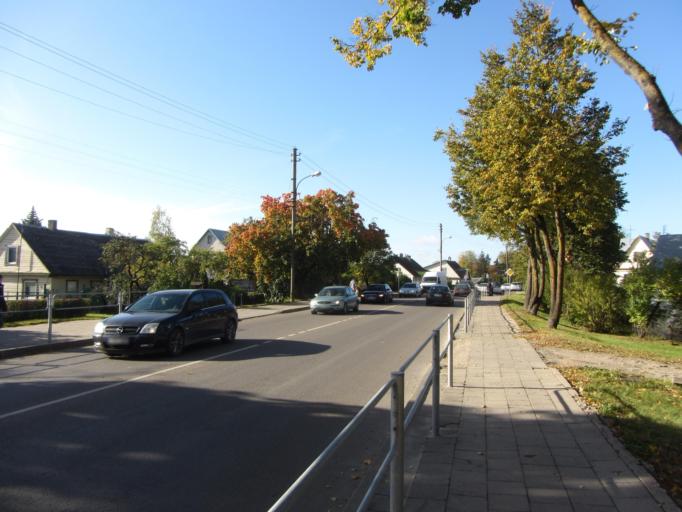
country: LT
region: Utenos apskritis
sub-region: Utena
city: Utena
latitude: 55.5009
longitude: 25.6132
